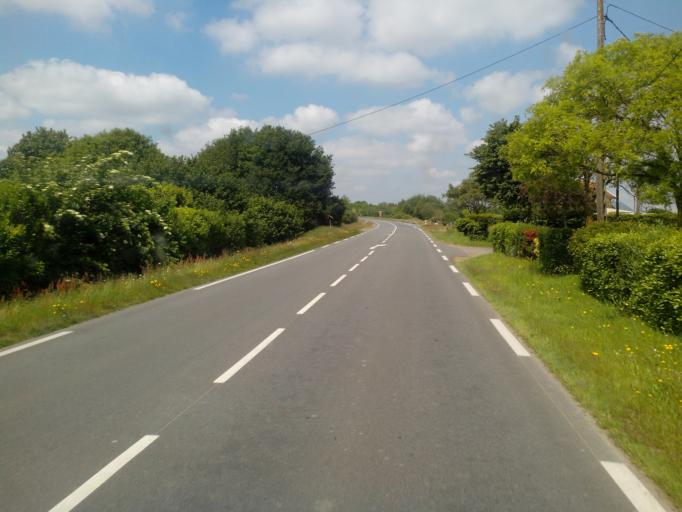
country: FR
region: Brittany
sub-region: Departement d'Ille-et-Vilaine
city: Saint-Germain-en-Cogles
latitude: 48.3958
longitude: -1.2949
